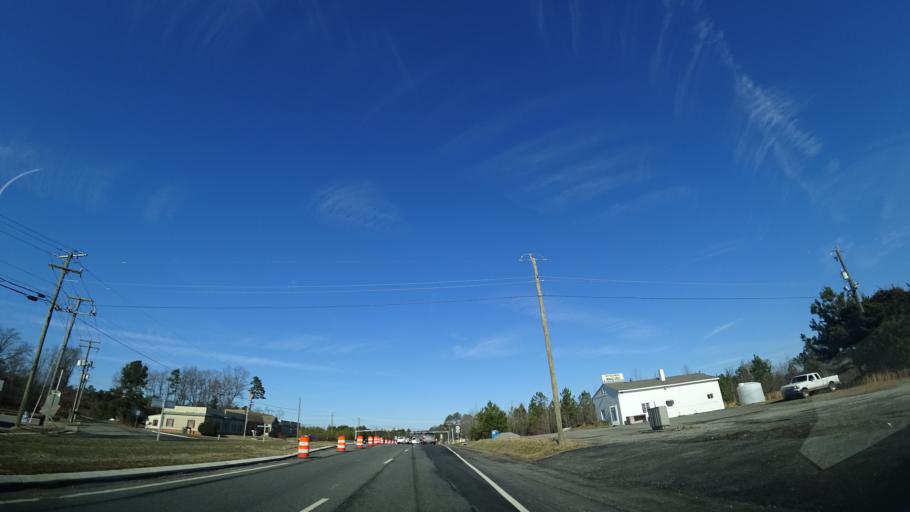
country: US
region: Virginia
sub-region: Henrico County
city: Glen Allen
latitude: 37.6886
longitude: -77.4625
